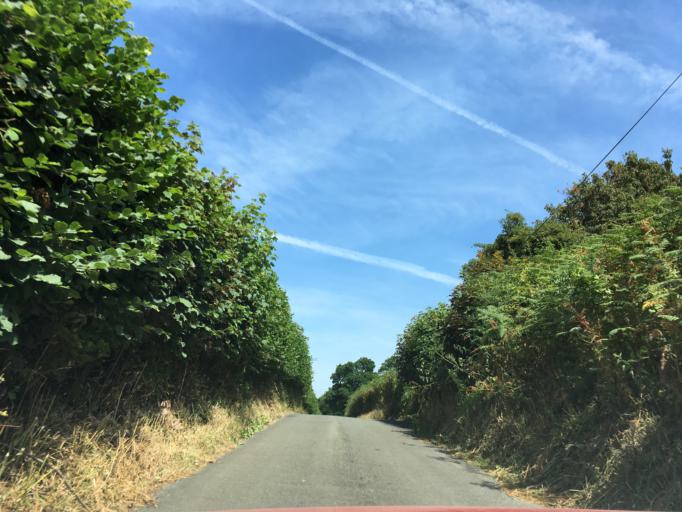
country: GB
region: Wales
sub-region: Caerphilly County Borough
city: Risca
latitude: 51.5906
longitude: -3.1082
